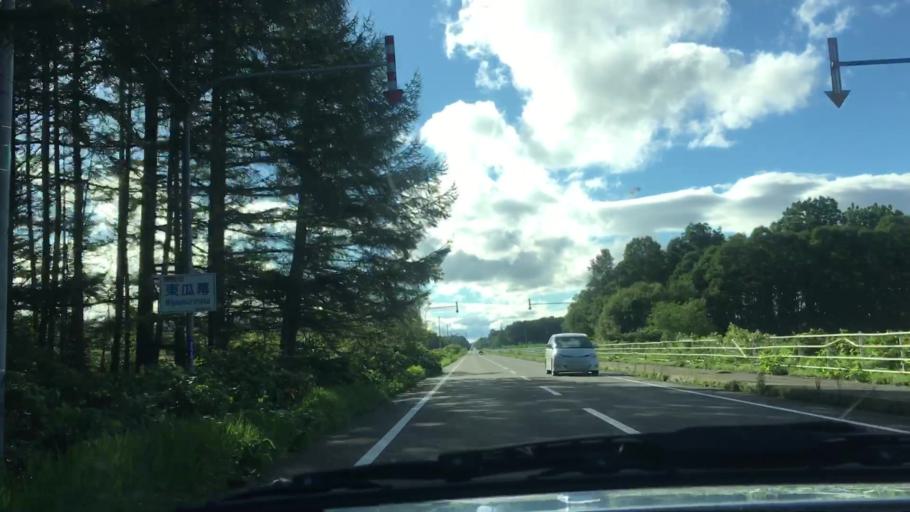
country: JP
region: Hokkaido
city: Otofuke
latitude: 43.1669
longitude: 143.1295
